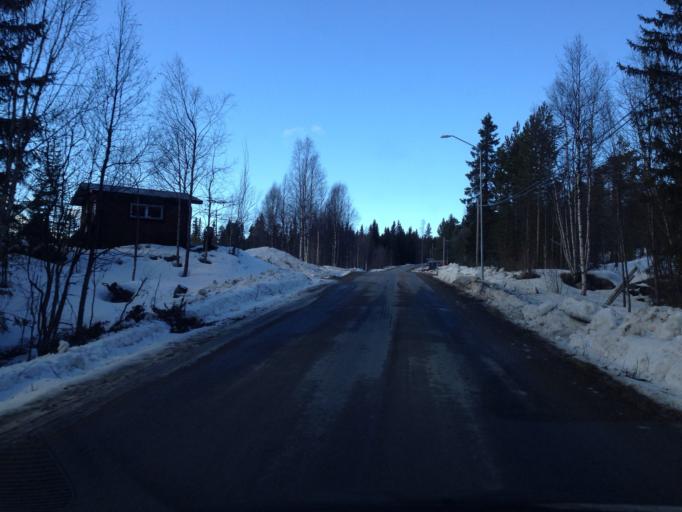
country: SE
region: Jaemtland
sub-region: Harjedalens Kommun
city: Sveg
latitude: 62.1187
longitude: 13.2704
